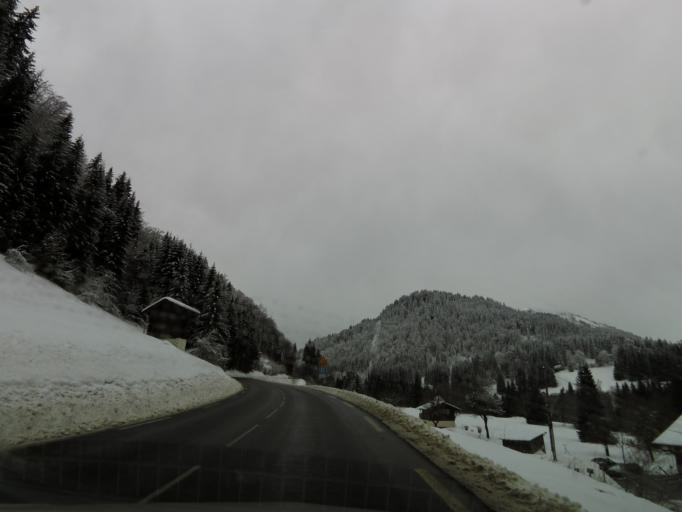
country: FR
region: Rhone-Alpes
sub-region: Departement de la Haute-Savoie
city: Morzine
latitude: 46.1868
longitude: 6.6828
